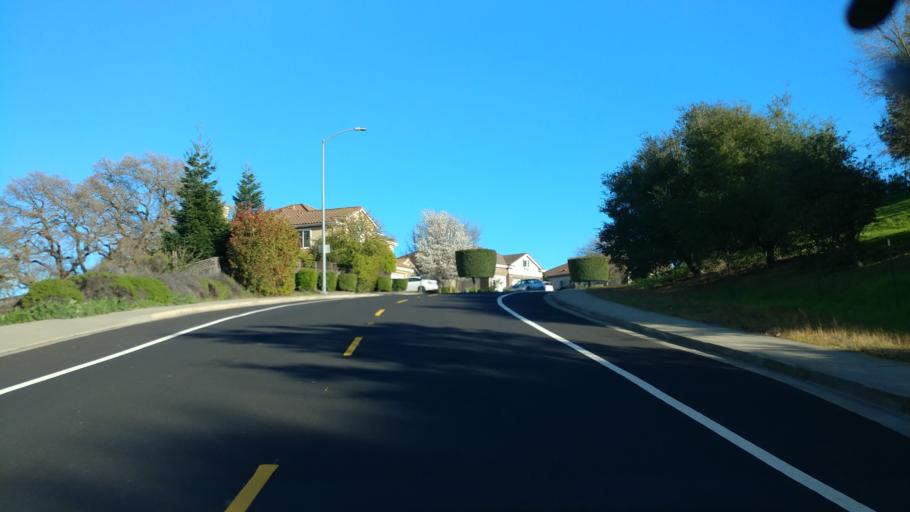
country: US
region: California
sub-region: Alameda County
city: Dublin
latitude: 37.7335
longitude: -121.9524
